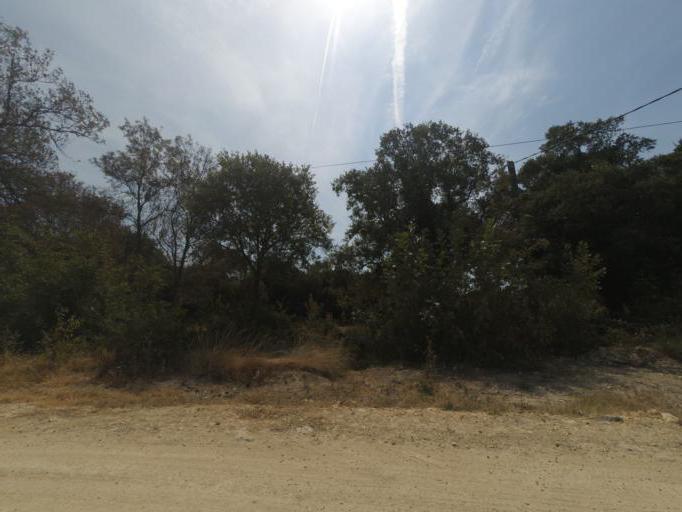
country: FR
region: Languedoc-Roussillon
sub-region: Departement du Gard
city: Aubais
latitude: 43.7644
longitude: 4.1185
